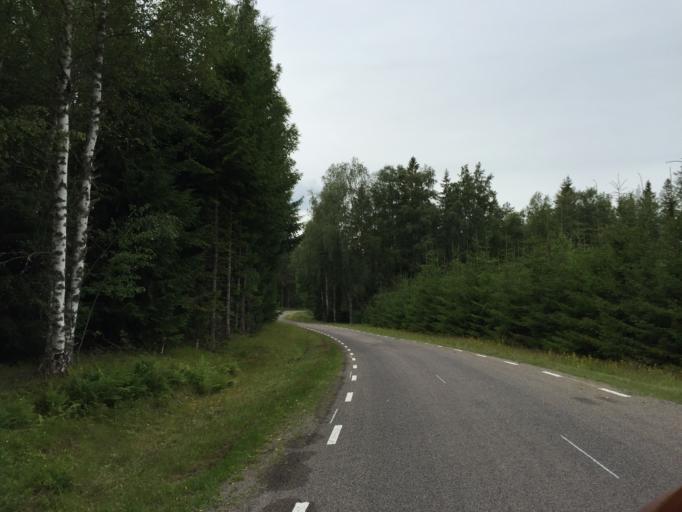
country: SE
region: Soedermanland
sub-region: Vingakers Kommun
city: Vingaker
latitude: 59.0089
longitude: 15.7146
